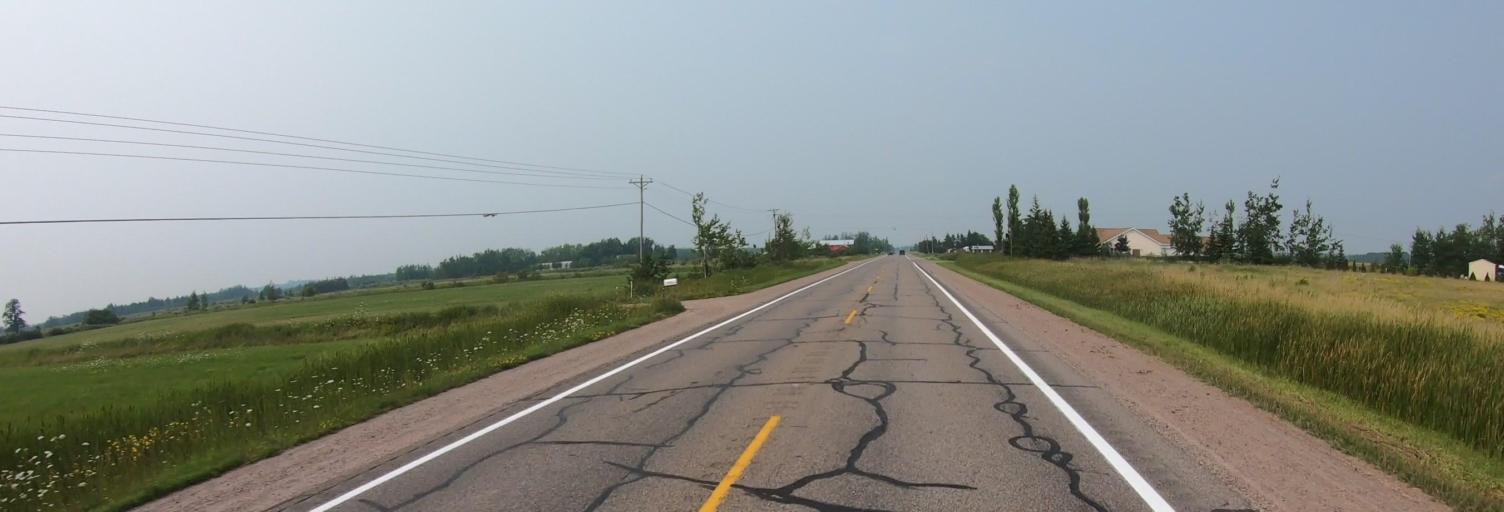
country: US
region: Michigan
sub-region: Chippewa County
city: Sault Ste. Marie
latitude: 46.4328
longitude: -84.3536
